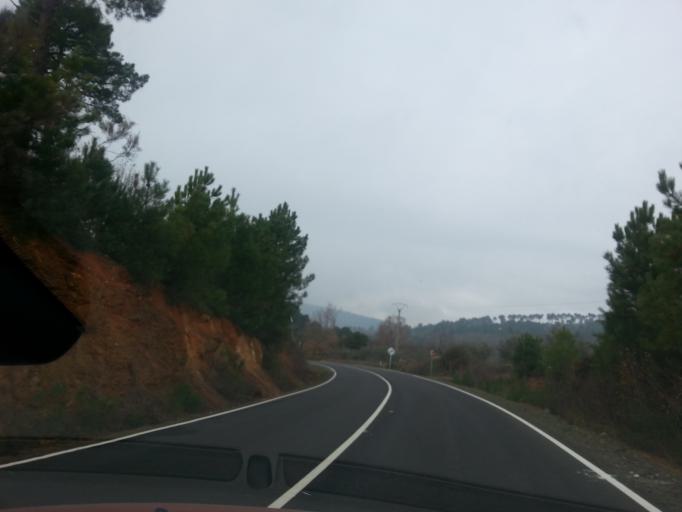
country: ES
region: Castille and Leon
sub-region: Provincia de Salamanca
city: Sotoserrano
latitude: 40.4429
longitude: -6.0488
